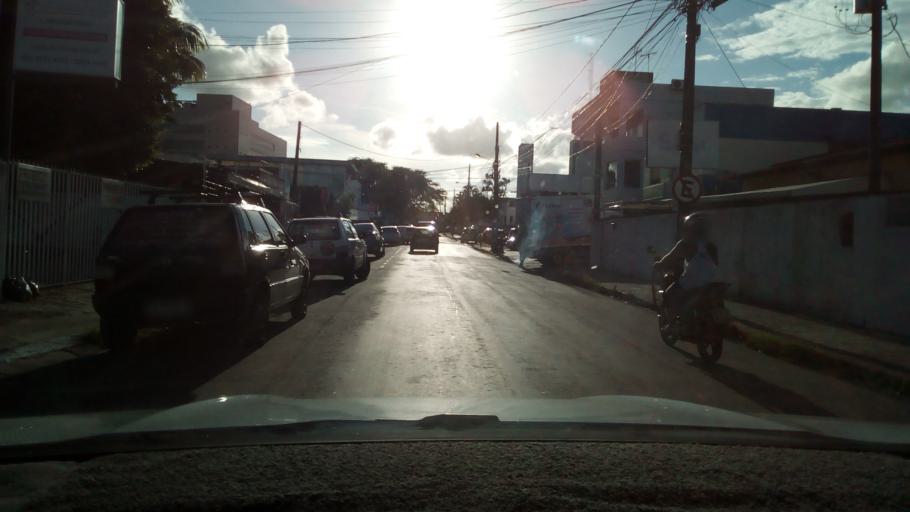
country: BR
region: Paraiba
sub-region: Joao Pessoa
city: Joao Pessoa
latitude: -7.1249
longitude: -34.8807
